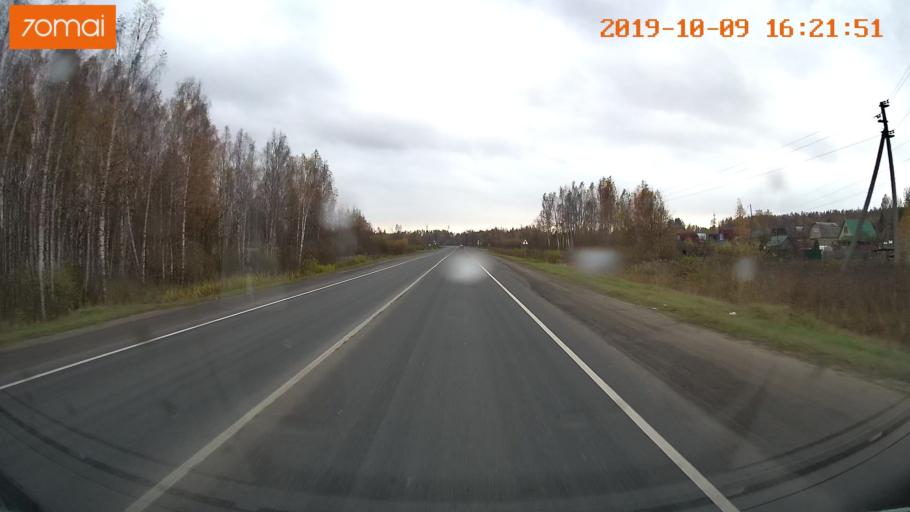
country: RU
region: Kostroma
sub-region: Kostromskoy Rayon
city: Kostroma
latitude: 57.6857
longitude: 40.8878
